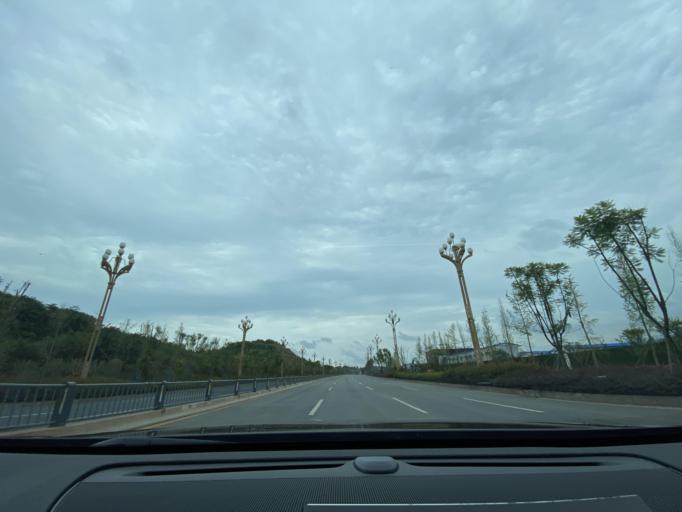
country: CN
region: Sichuan
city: Jiancheng
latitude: 30.4849
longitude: 104.4805
